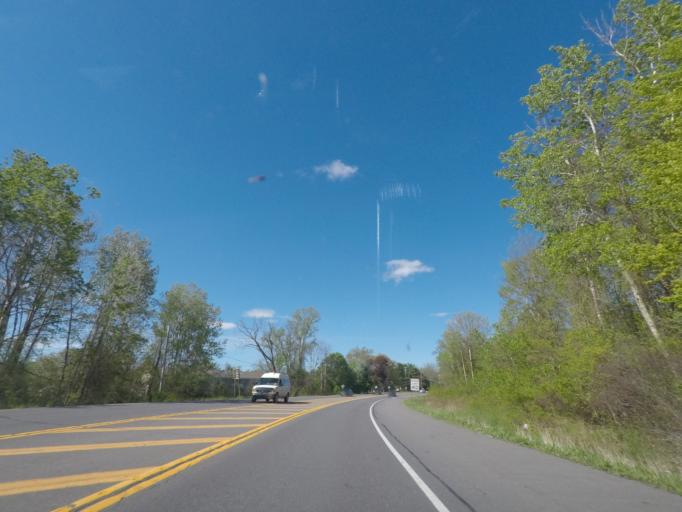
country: US
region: New York
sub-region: Albany County
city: Delmar
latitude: 42.5755
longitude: -73.8034
